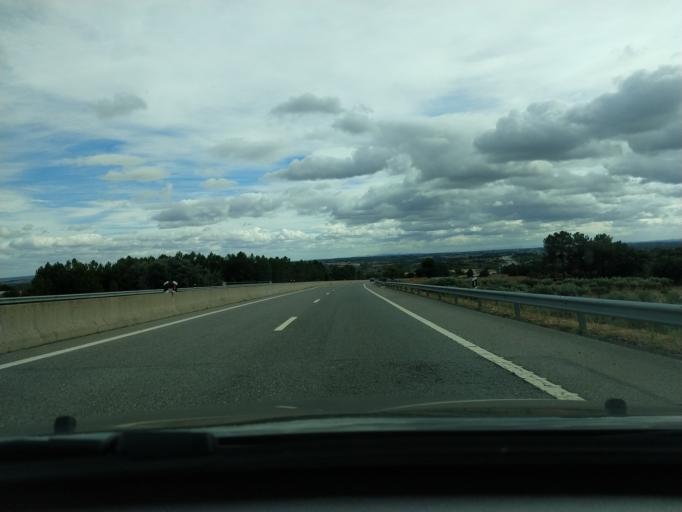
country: PT
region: Castelo Branco
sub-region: Concelho do Fundao
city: Fundao
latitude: 40.0459
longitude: -7.4720
